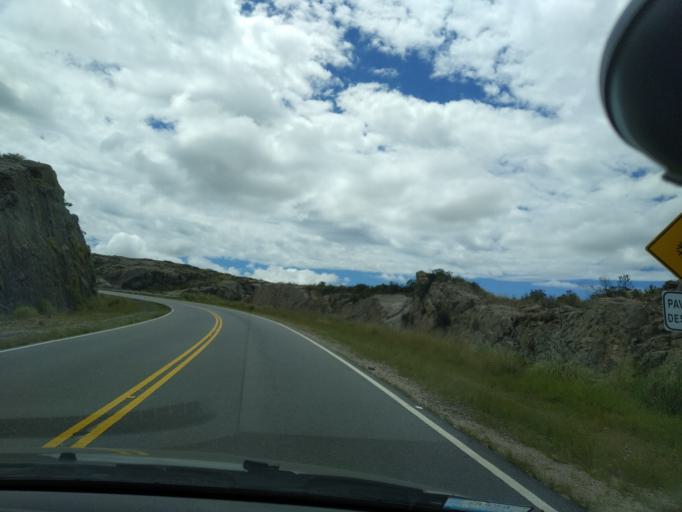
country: AR
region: Cordoba
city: Villa Cura Brochero
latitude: -31.6190
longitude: -64.8924
